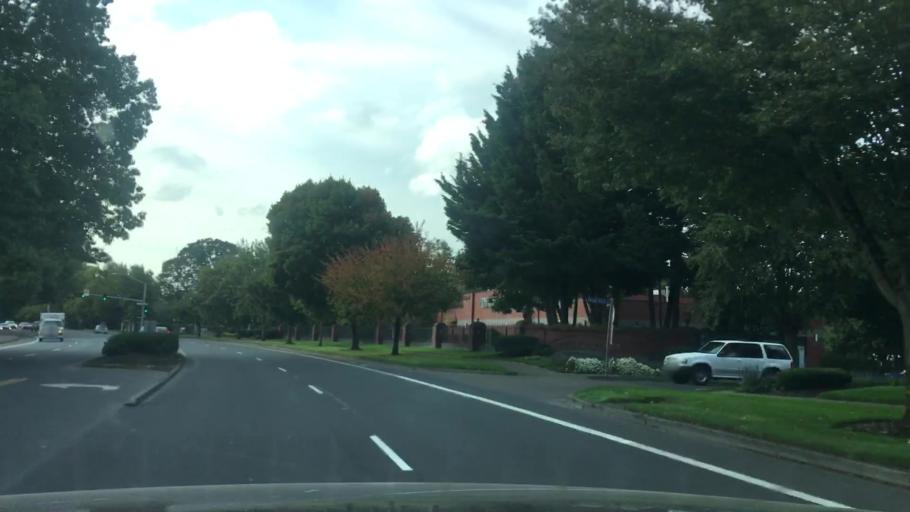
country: US
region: Oregon
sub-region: Lane County
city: Eugene
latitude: 44.0865
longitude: -123.1051
